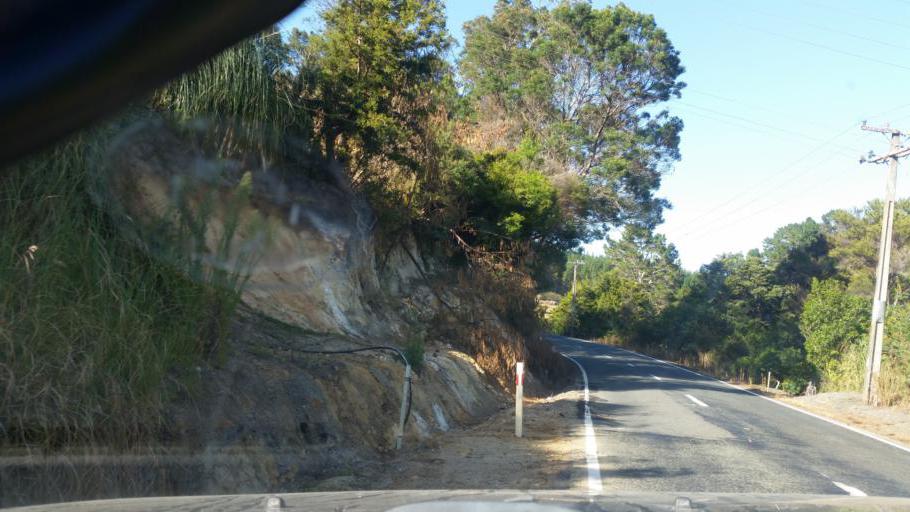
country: NZ
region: Northland
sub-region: Kaipara District
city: Dargaville
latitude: -35.8133
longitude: 173.7272
